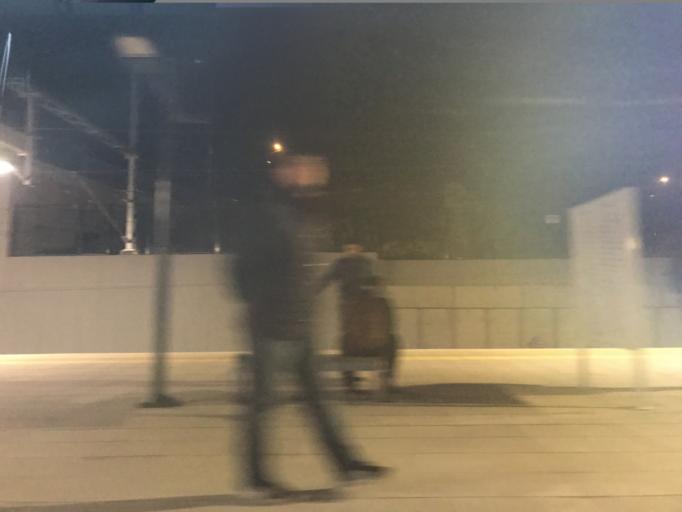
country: TR
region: Istanbul
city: Maltepe
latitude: 40.9100
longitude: 29.1560
